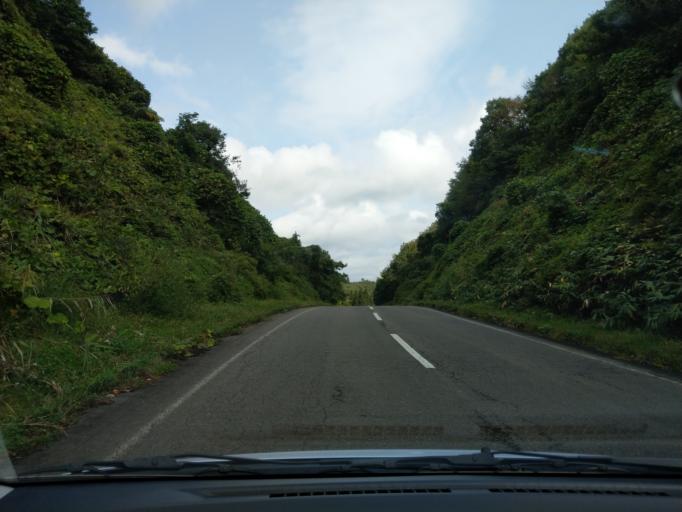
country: JP
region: Akita
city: Omagari
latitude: 39.4767
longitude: 140.3091
